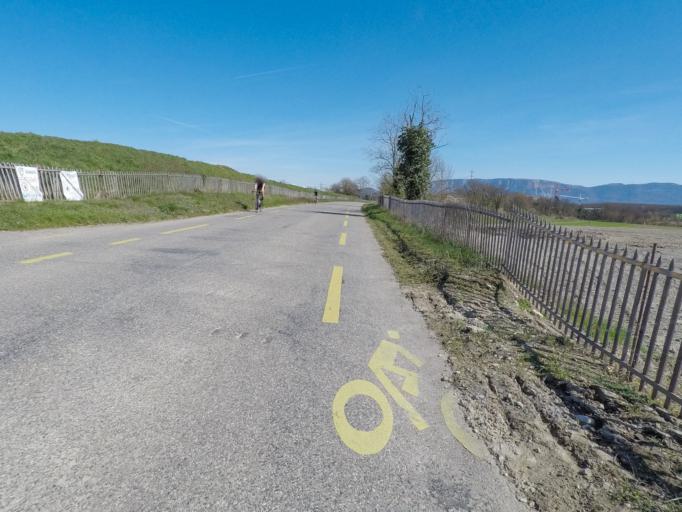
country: CH
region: Geneva
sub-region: Geneva
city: Aire-la-Ville
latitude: 46.2025
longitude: 6.0511
